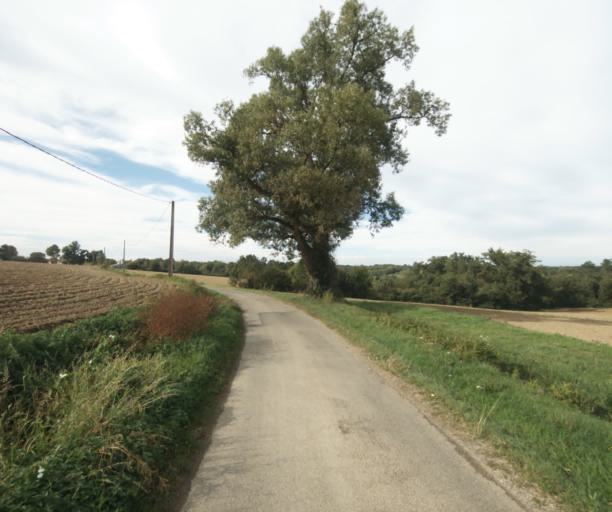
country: FR
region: Midi-Pyrenees
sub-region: Departement du Gers
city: Le Houga
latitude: 43.8642
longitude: -0.1387
